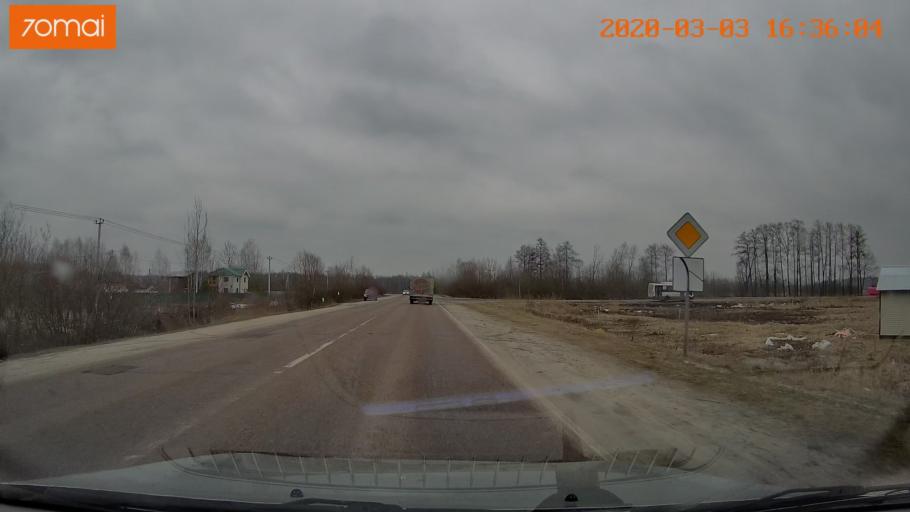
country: RU
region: Moskovskaya
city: Lopatinskiy
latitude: 55.4007
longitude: 38.7681
